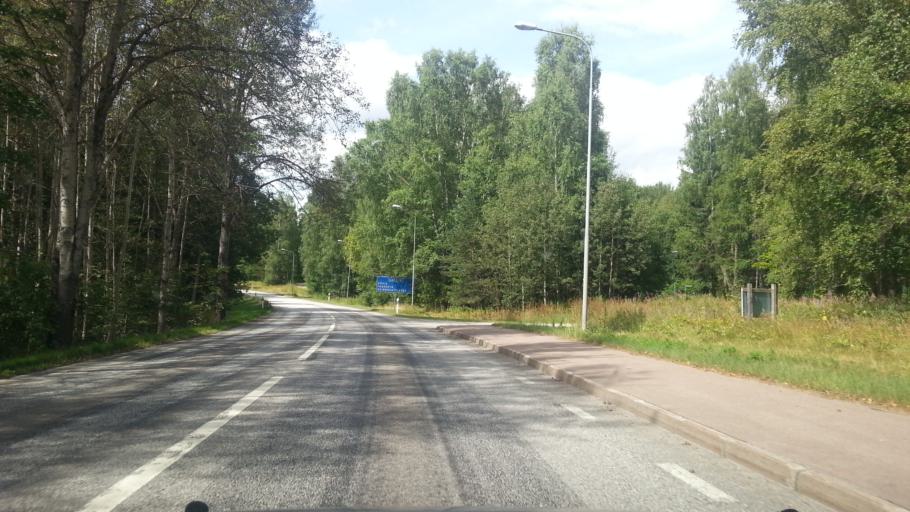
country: SE
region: Vaestmanland
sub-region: Skinnskattebergs Kommun
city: Skinnskatteberg
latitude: 59.8091
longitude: 15.5398
